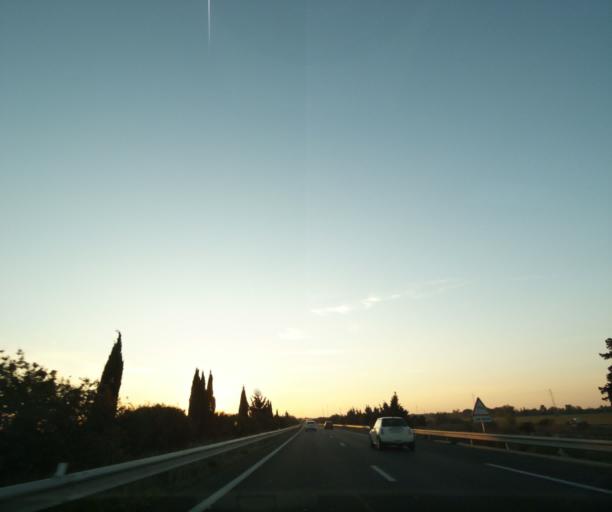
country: FR
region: Provence-Alpes-Cote d'Azur
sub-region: Departement des Bouches-du-Rhone
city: Mouries
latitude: 43.6390
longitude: 4.8688
